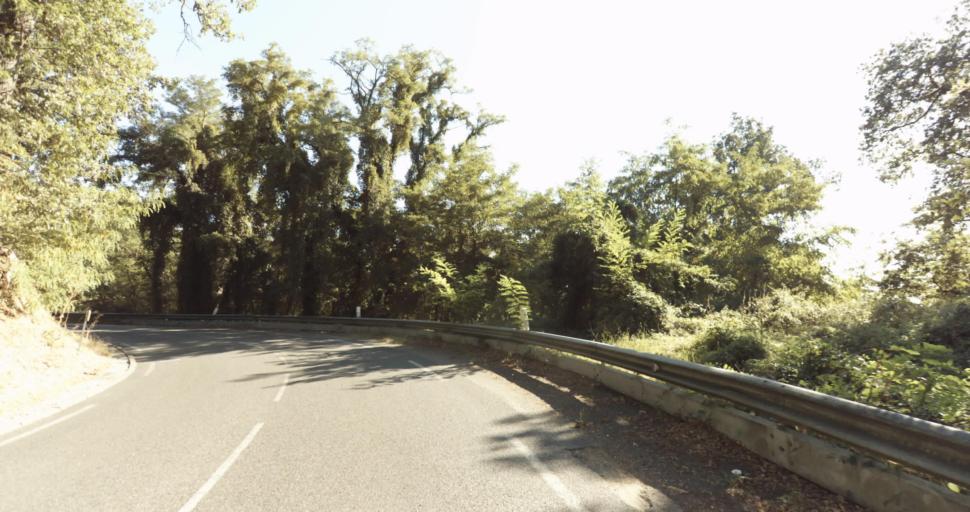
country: FR
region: Midi-Pyrenees
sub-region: Departement de la Haute-Garonne
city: Saint-Genies-Bellevue
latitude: 43.6741
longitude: 1.4782
